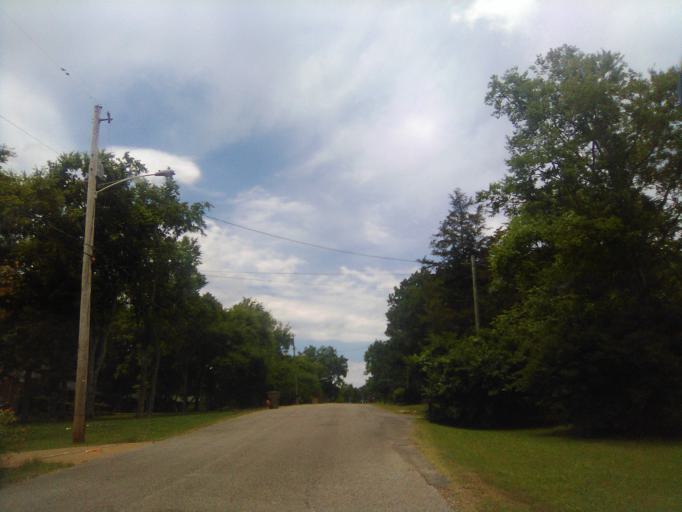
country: US
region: Tennessee
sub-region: Davidson County
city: Belle Meade
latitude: 36.1282
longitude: -86.8867
